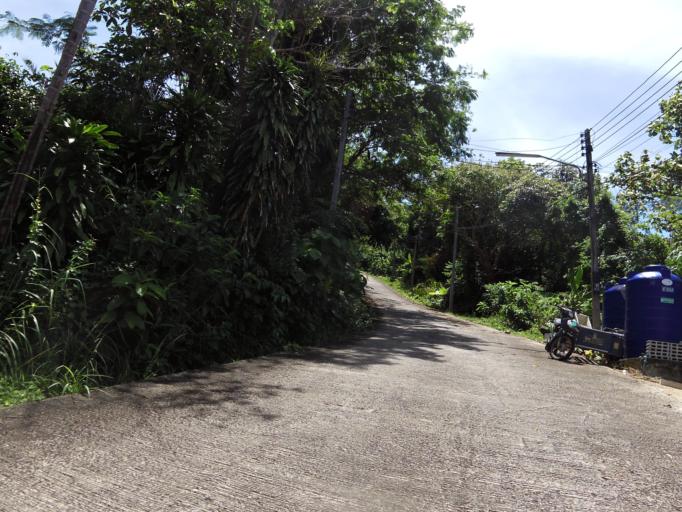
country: TH
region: Phuket
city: Ban Karon
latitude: 7.8470
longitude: 98.3048
